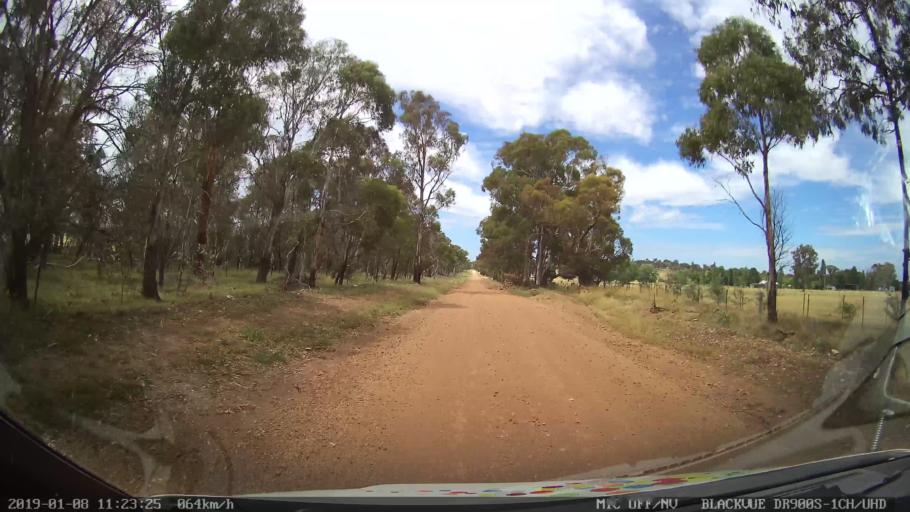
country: AU
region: New South Wales
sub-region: Guyra
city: Guyra
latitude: -30.2550
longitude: 151.5590
